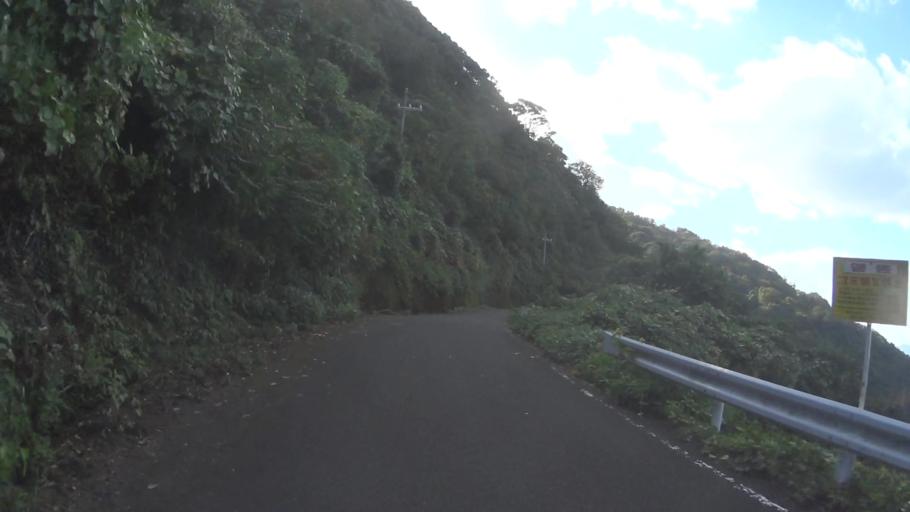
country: JP
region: Kyoto
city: Maizuru
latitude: 35.5679
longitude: 135.4181
